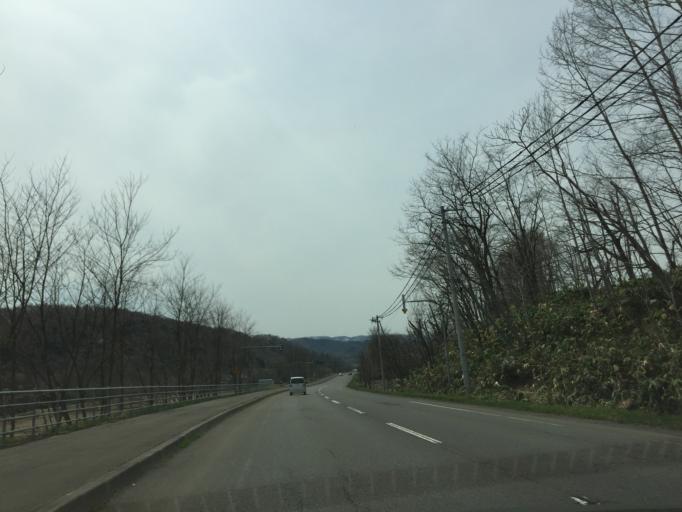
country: JP
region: Hokkaido
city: Ashibetsu
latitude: 43.5518
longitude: 142.1779
